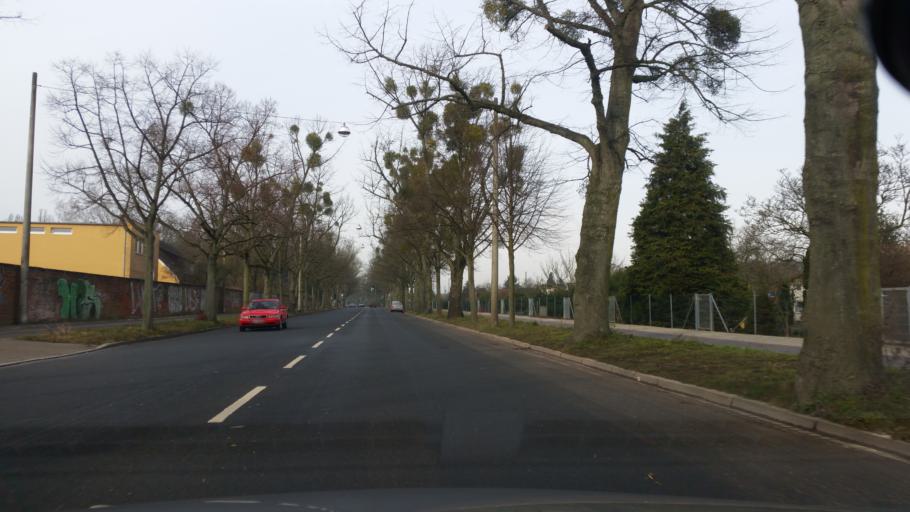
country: DE
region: Lower Saxony
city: Hannover
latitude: 52.3953
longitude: 9.7044
